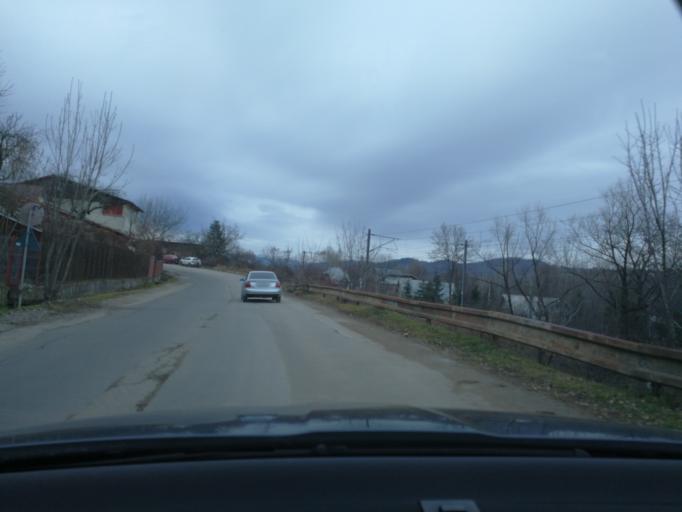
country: RO
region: Prahova
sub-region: Comuna Poiana Campina
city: Poiana Campina
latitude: 45.1430
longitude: 25.6948
